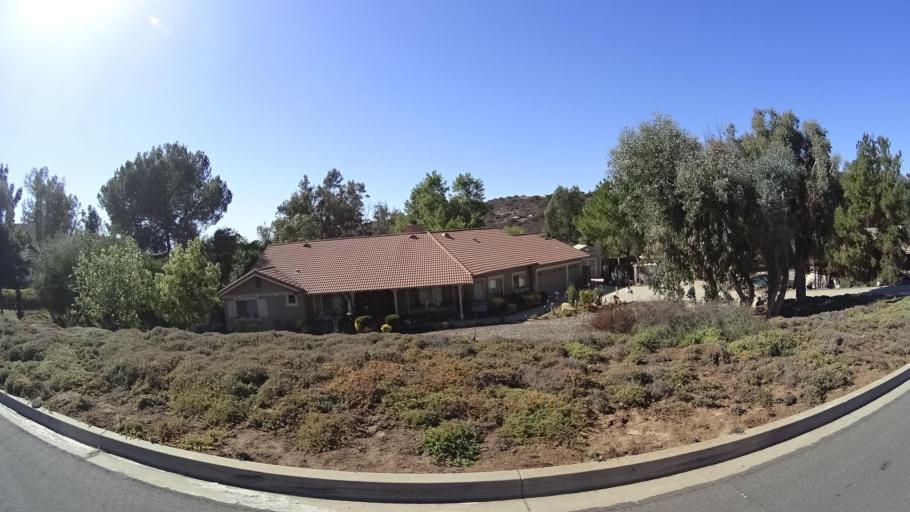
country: US
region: California
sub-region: San Diego County
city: Lakeside
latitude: 32.8622
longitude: -116.8738
